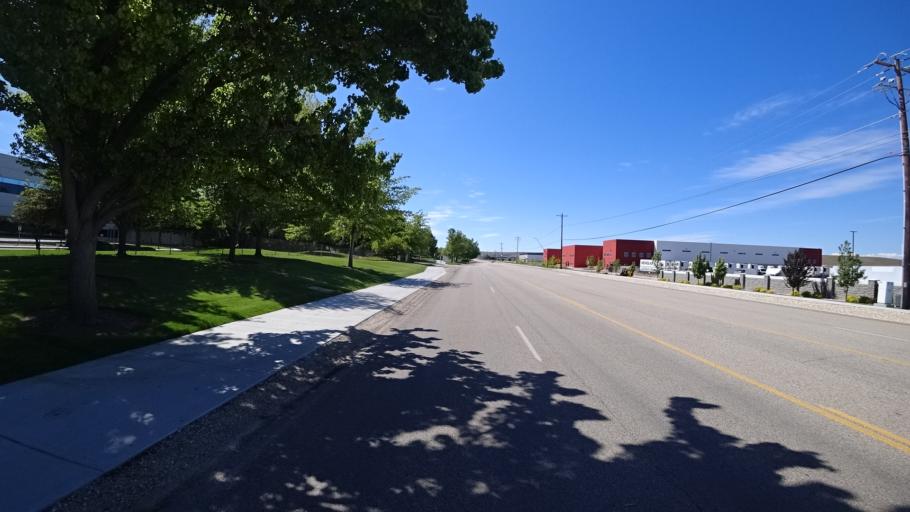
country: US
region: Idaho
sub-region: Ada County
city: Boise
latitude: 43.5268
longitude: -116.1493
